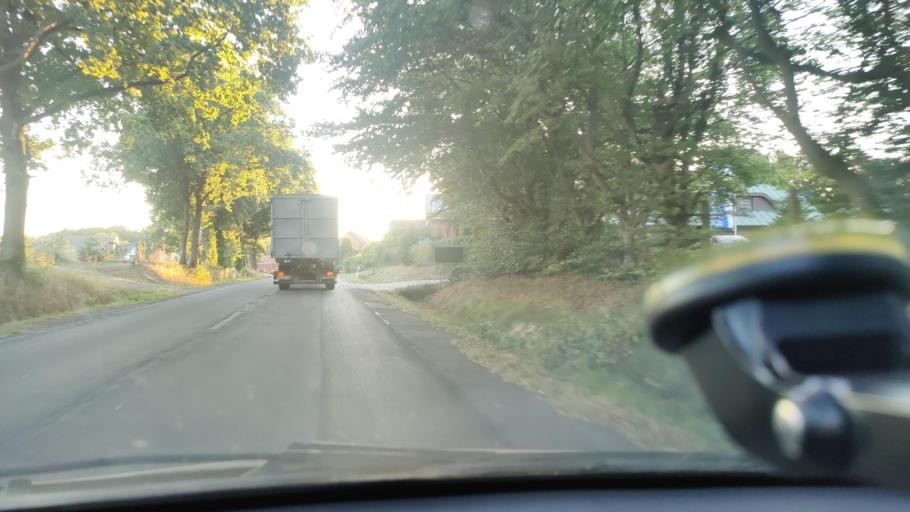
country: DE
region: North Rhine-Westphalia
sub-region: Regierungsbezirk Munster
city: Klein Reken
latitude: 51.7829
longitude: 7.0189
